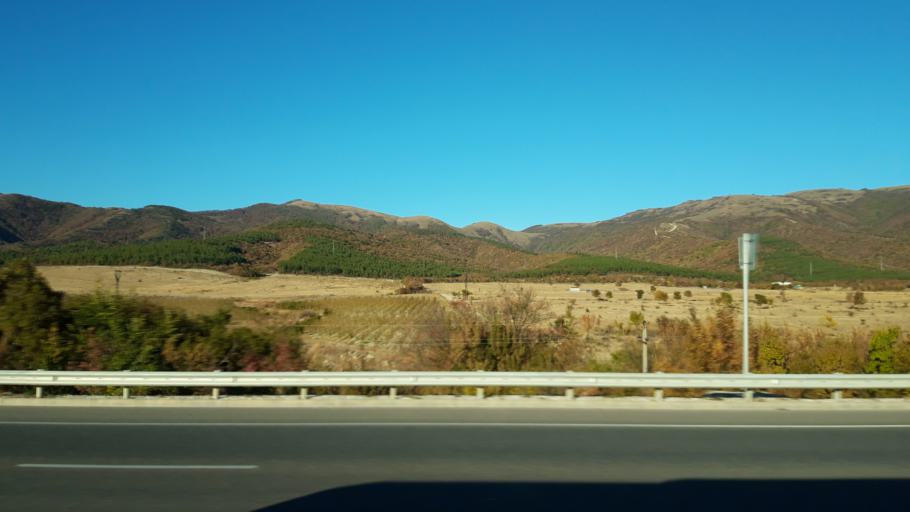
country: RU
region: Krasnodarskiy
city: Kabardinka
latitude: 44.6376
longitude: 37.9891
